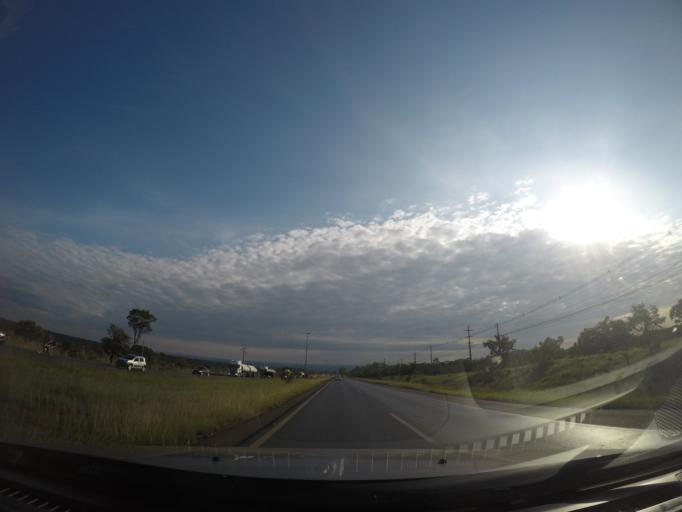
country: BR
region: Goias
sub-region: Planaltina
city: Planaltina
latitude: -15.6312
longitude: -47.7346
